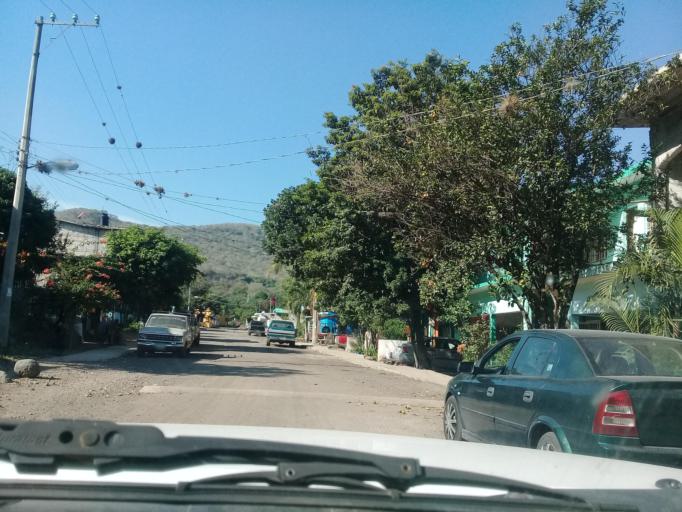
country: MX
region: Veracruz
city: Actopan
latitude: 19.4977
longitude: -96.6075
